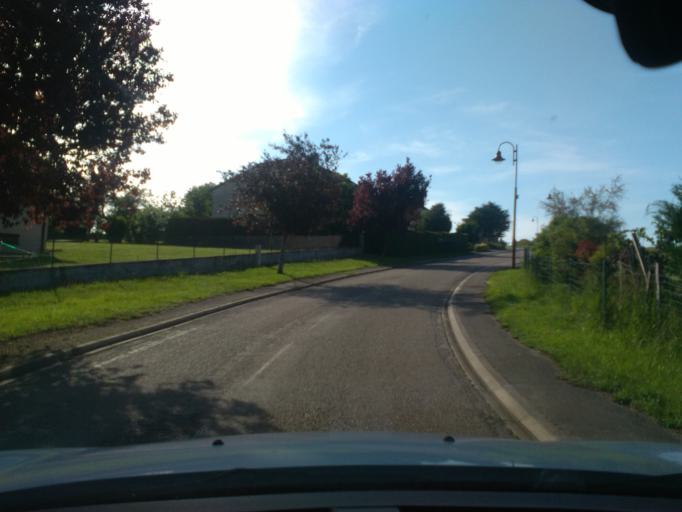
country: FR
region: Lorraine
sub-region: Departement des Vosges
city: Mirecourt
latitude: 48.2873
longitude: 6.1687
